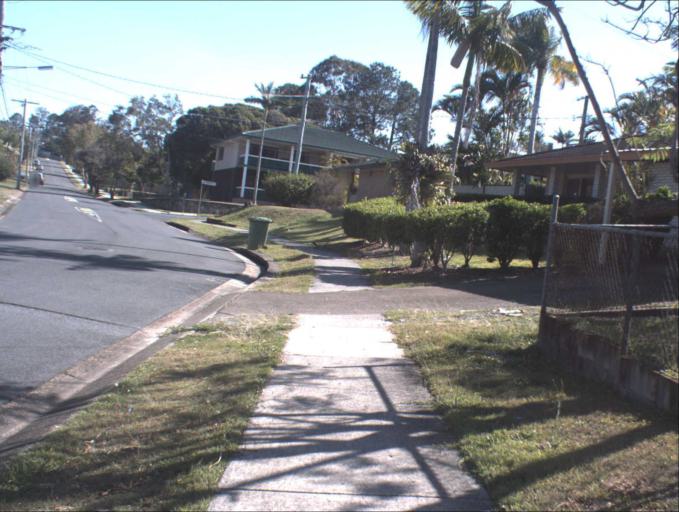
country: AU
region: Queensland
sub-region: Logan
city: Rochedale South
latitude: -27.5935
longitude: 153.1309
